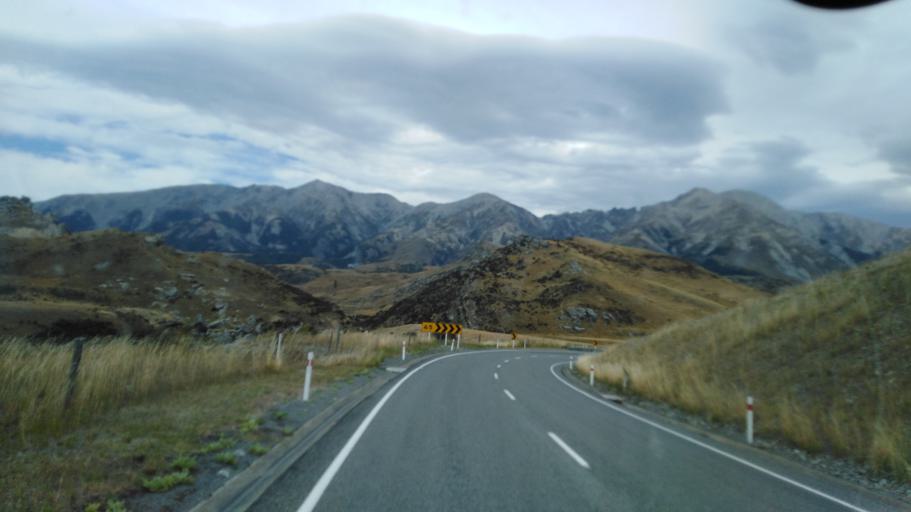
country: NZ
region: Canterbury
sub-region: Ashburton District
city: Methven
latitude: -43.1945
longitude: 171.7398
